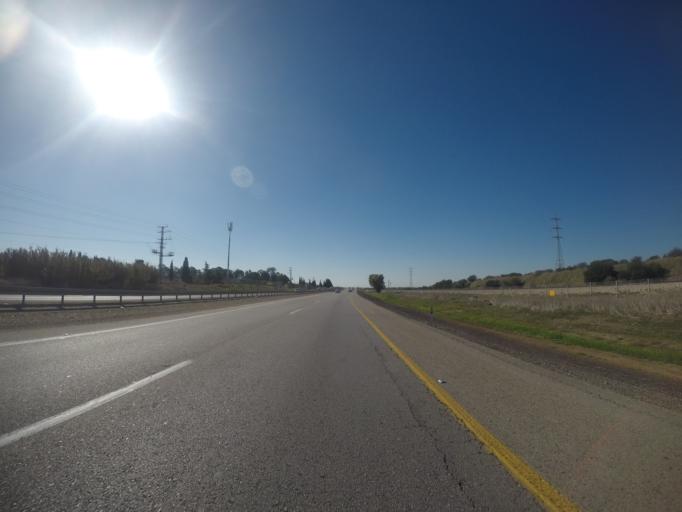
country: IL
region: Southern District
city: Ashdod
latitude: 31.7362
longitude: 34.6427
